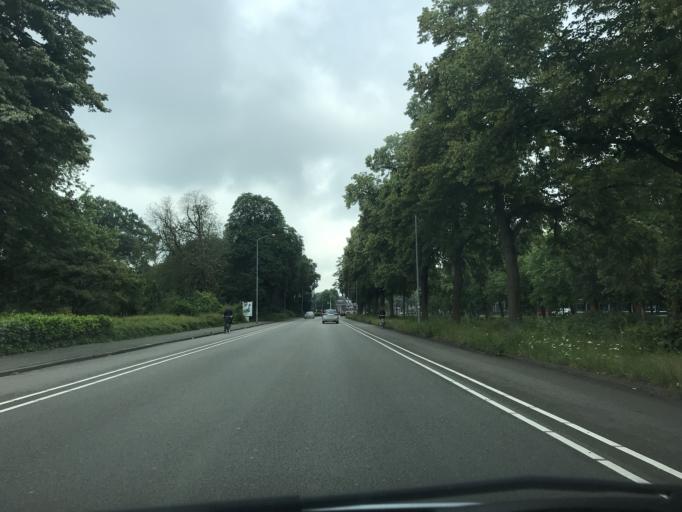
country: NL
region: North Brabant
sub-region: Gemeente Breda
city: Breda
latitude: 51.5842
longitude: 4.7839
